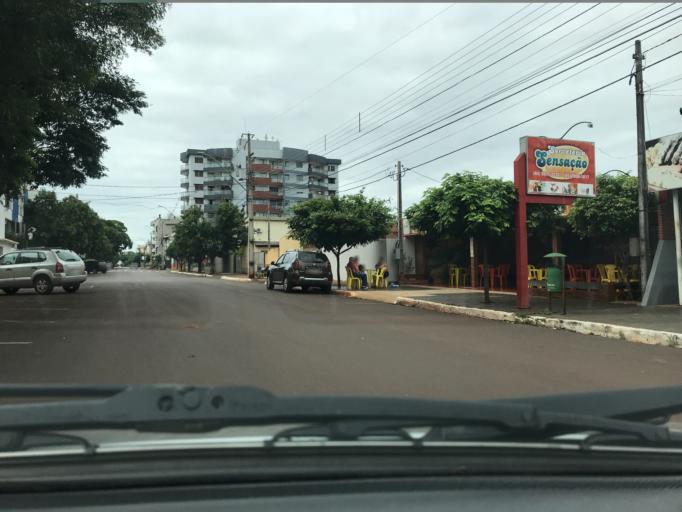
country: BR
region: Parana
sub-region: Palotina
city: Palotina
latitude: -24.2847
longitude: -53.8408
